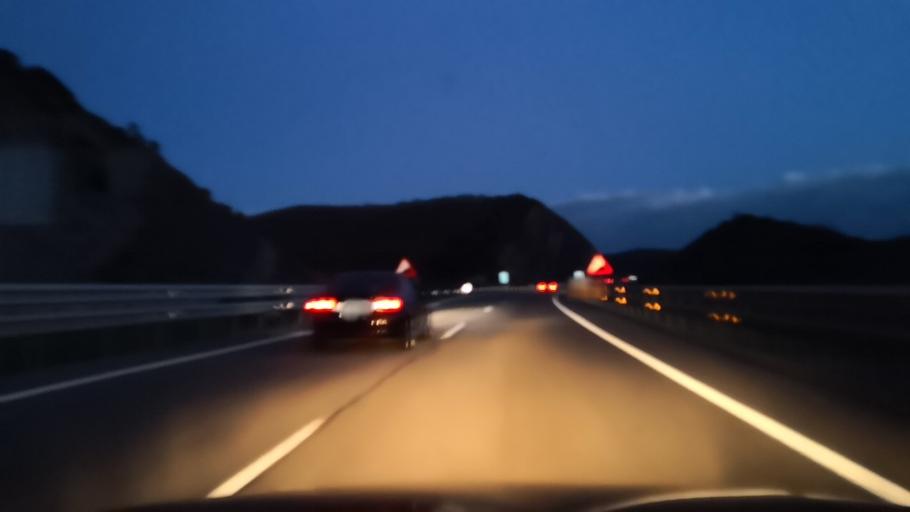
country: ES
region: Castille and Leon
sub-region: Provincia de Leon
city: Folgoso de la Ribera
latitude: 42.6196
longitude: -6.2804
